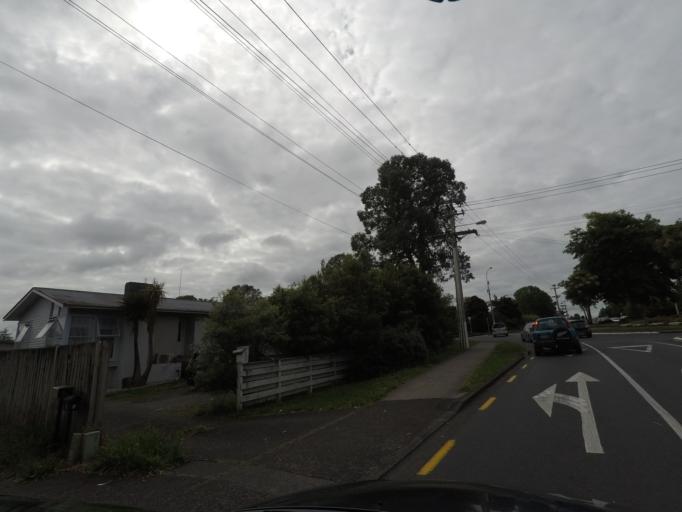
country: NZ
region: Auckland
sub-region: Auckland
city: Rosebank
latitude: -36.8603
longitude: 174.6116
